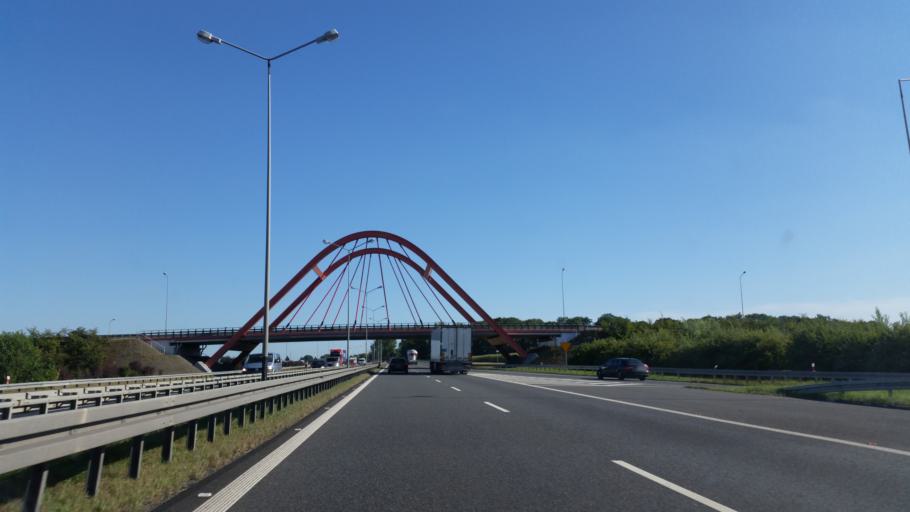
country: PL
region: Lower Silesian Voivodeship
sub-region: Powiat wroclawski
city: Zorawina
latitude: 50.9708
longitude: 17.0640
